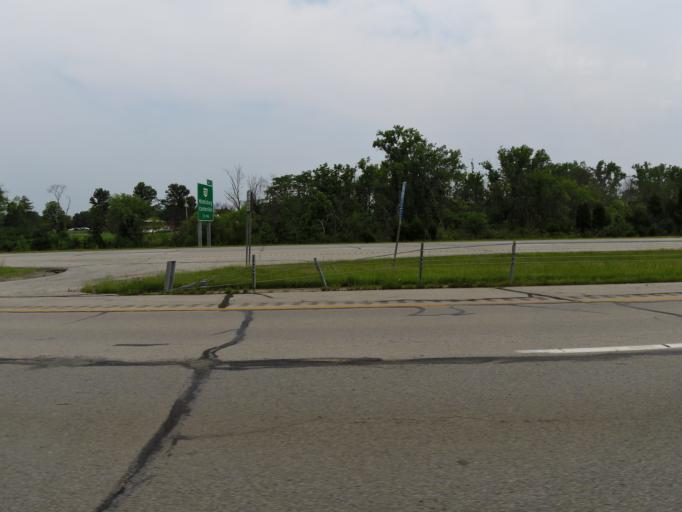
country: US
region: Ohio
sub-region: Montgomery County
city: Centerville
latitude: 39.6362
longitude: -84.1834
